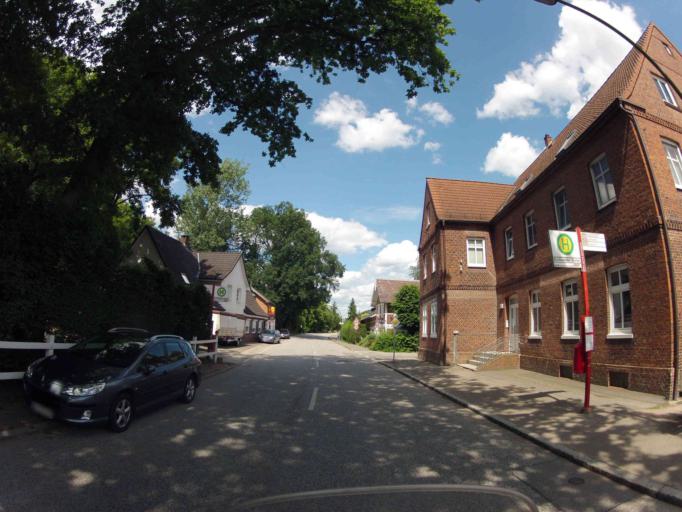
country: DE
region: Lower Saxony
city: Winsen
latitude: 53.4185
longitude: 10.1994
